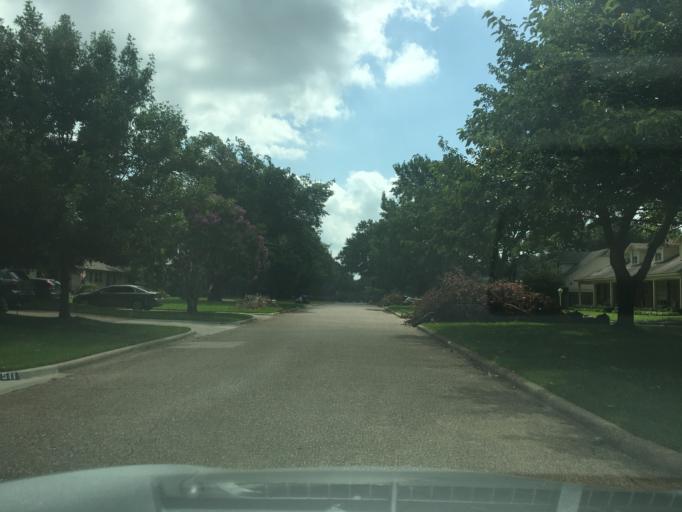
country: US
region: Texas
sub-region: Dallas County
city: Addison
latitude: 32.9132
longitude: -96.8314
